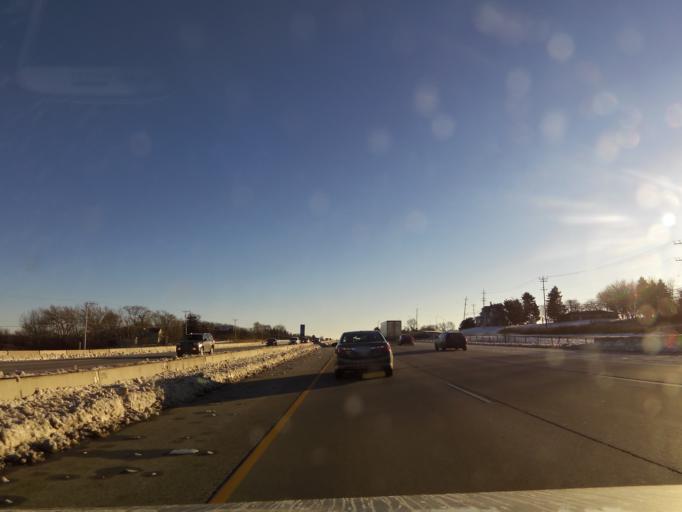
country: US
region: Wisconsin
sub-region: Racine County
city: Caledonia
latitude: 42.7994
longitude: -87.9533
